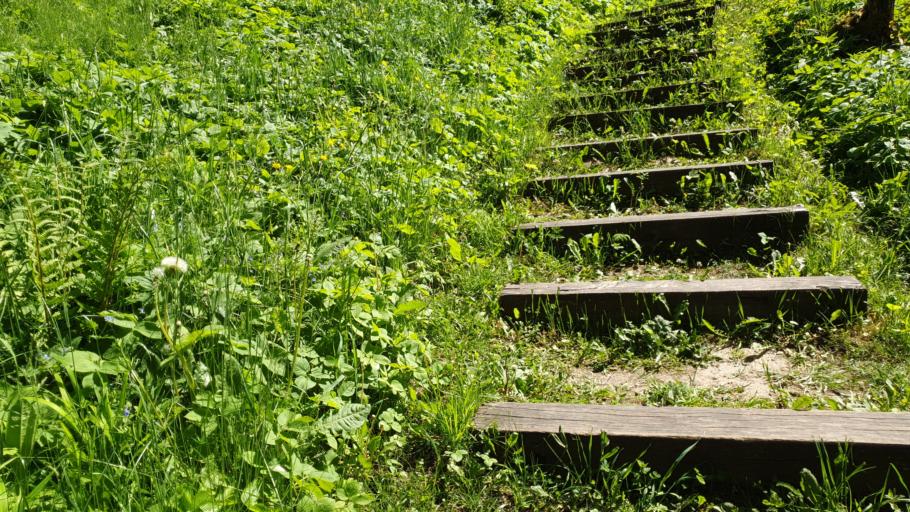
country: LT
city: Moletai
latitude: 55.0734
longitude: 25.4156
